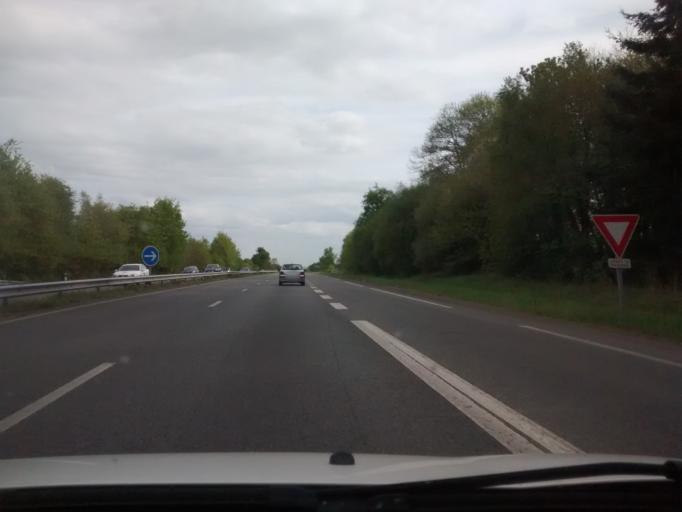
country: FR
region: Brittany
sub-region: Departement d'Ille-et-Vilaine
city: Saint-Pierre-de-Plesguen
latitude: 48.4273
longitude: -1.9130
